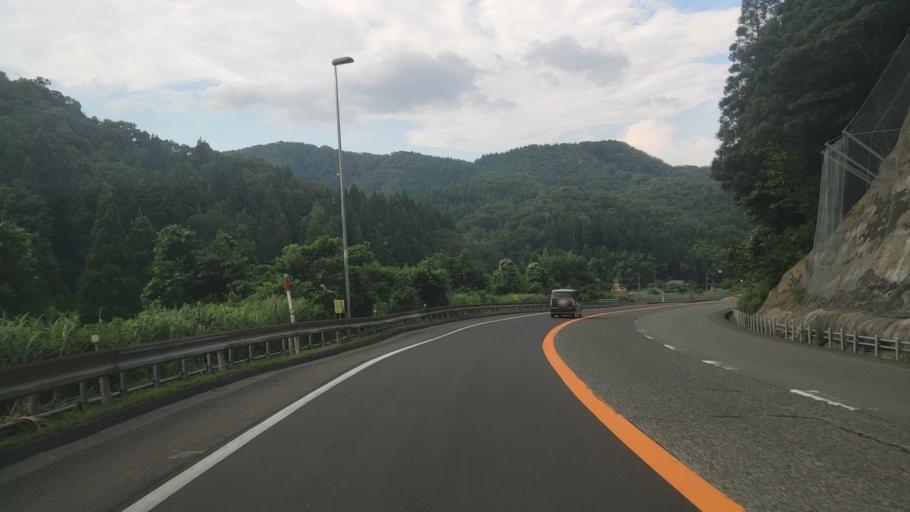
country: JP
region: Fukui
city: Takefu
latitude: 35.8517
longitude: 136.1284
